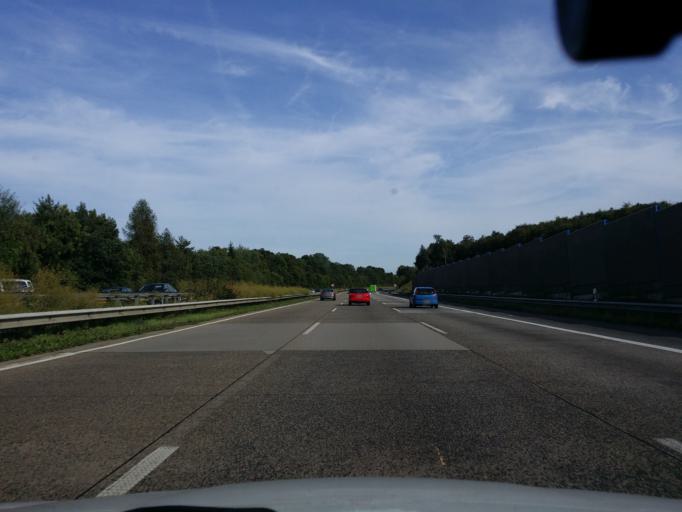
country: DE
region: Rheinland-Pfalz
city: Rossbach
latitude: 50.6160
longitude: 7.4181
